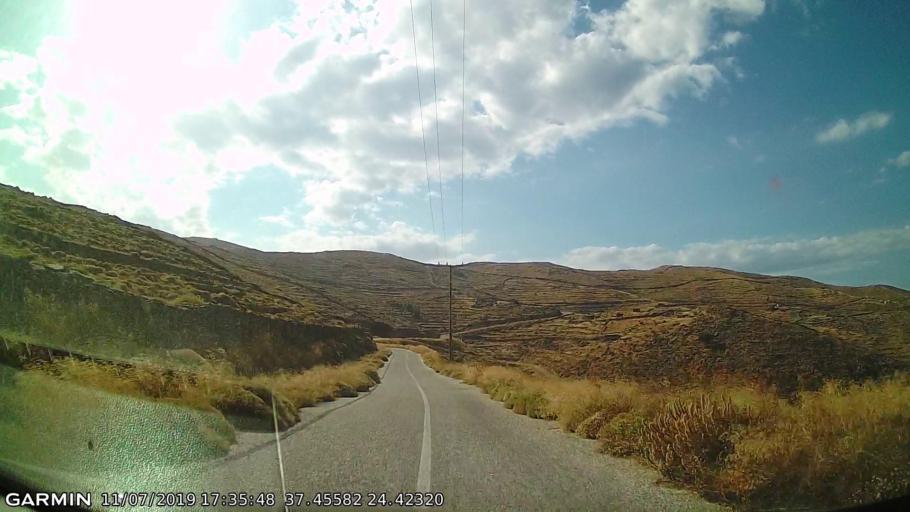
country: GR
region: South Aegean
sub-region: Nomos Kykladon
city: Kythnos
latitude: 37.4558
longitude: 24.4228
